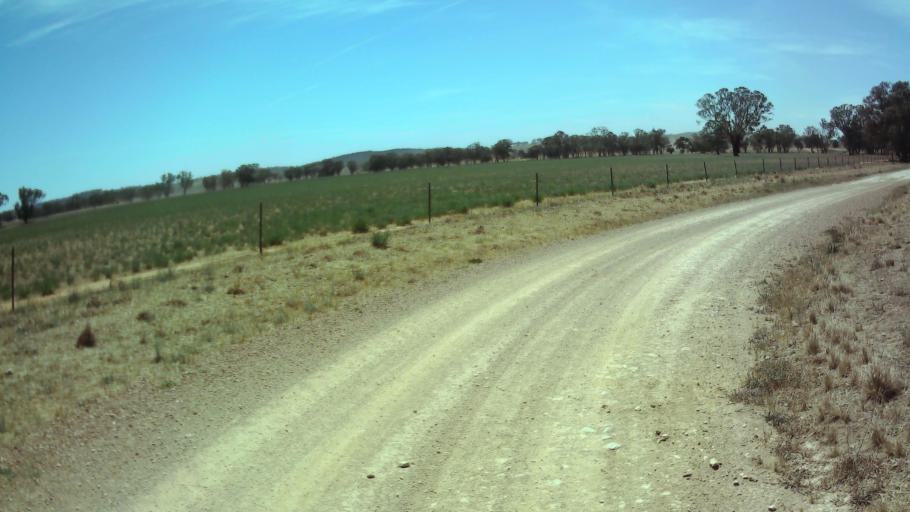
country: AU
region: New South Wales
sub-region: Weddin
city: Grenfell
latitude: -33.9919
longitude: 148.1571
